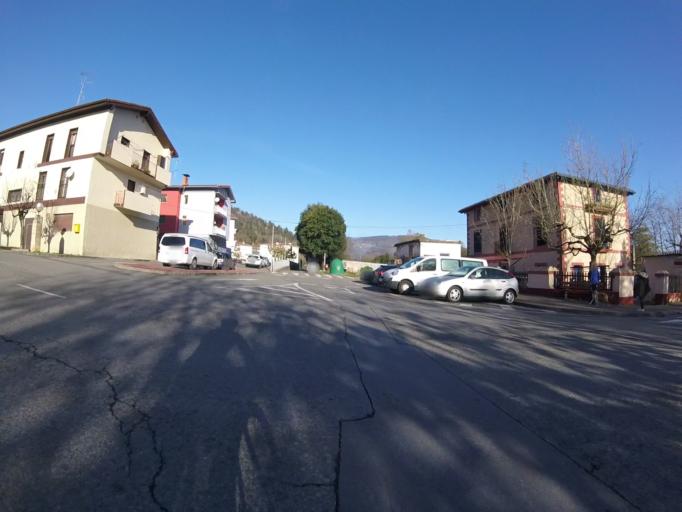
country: ES
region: Basque Country
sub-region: Provincia de Guipuzcoa
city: Usurbil
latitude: 43.2661
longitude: -2.0561
